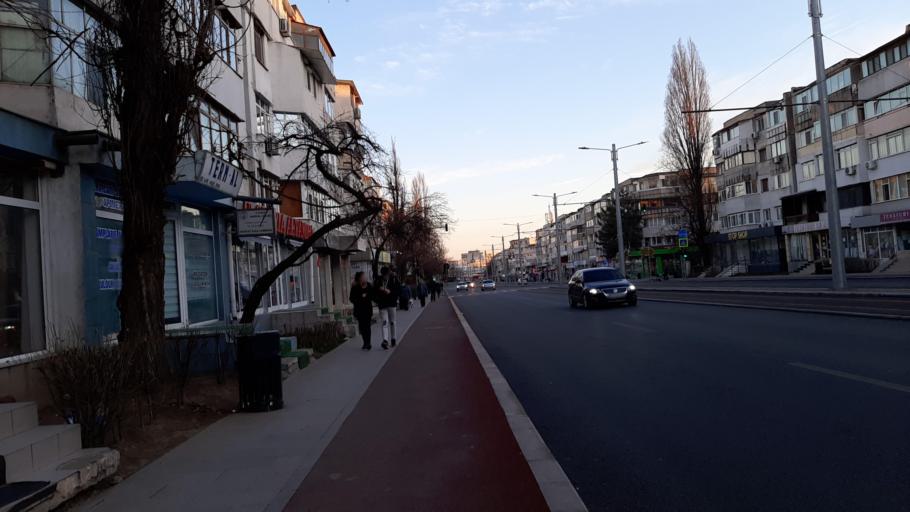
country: RO
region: Galati
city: Galati
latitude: 45.4386
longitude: 28.0224
